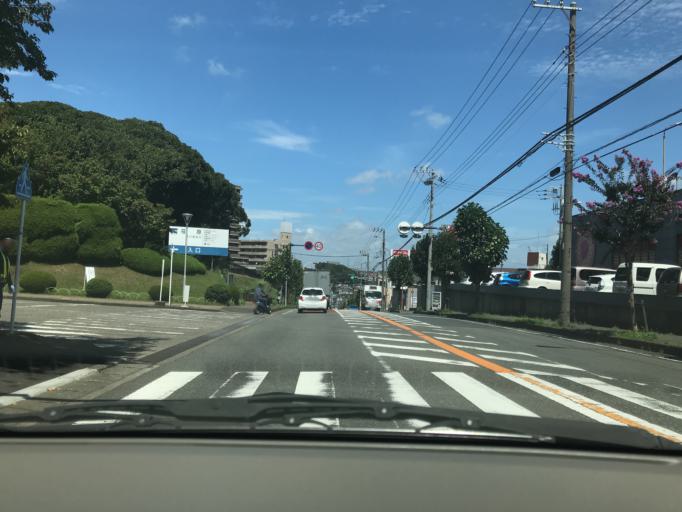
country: JP
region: Kanagawa
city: Fujisawa
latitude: 35.3578
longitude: 139.4677
